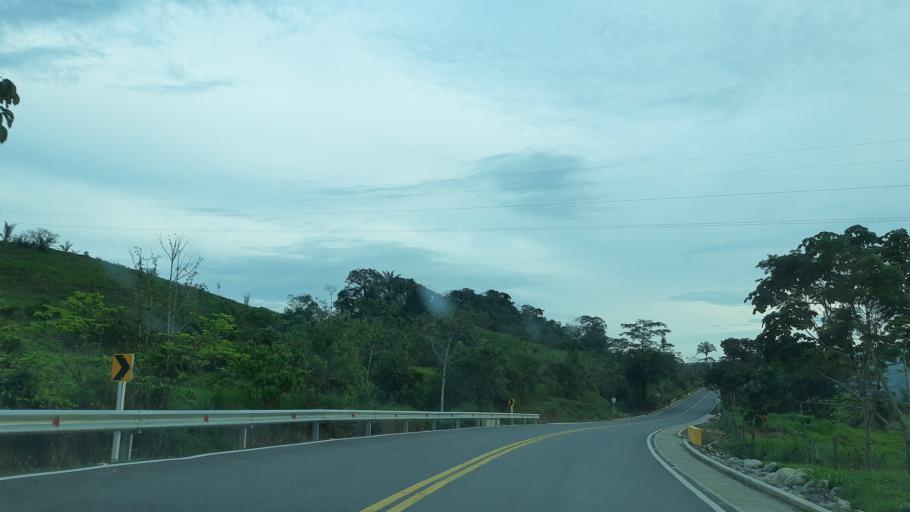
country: CO
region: Casanare
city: Sabanalarga
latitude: 4.8093
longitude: -73.0589
